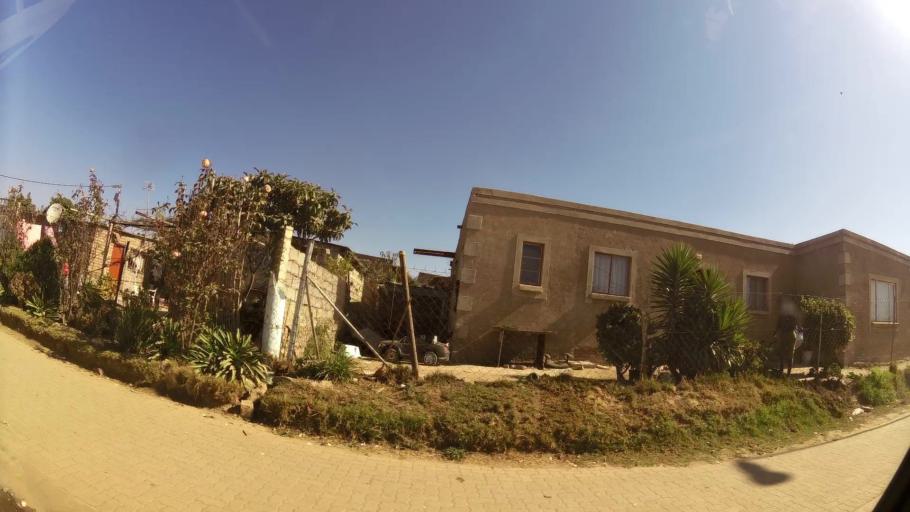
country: ZA
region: Gauteng
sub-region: City of Johannesburg Metropolitan Municipality
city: Midrand
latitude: -25.9221
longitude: 28.0917
